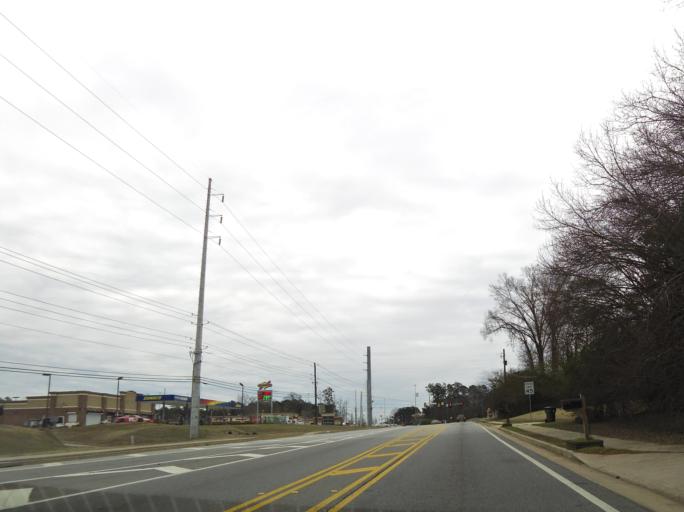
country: US
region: Georgia
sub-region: Bibb County
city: West Point
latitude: 32.8806
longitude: -83.7756
